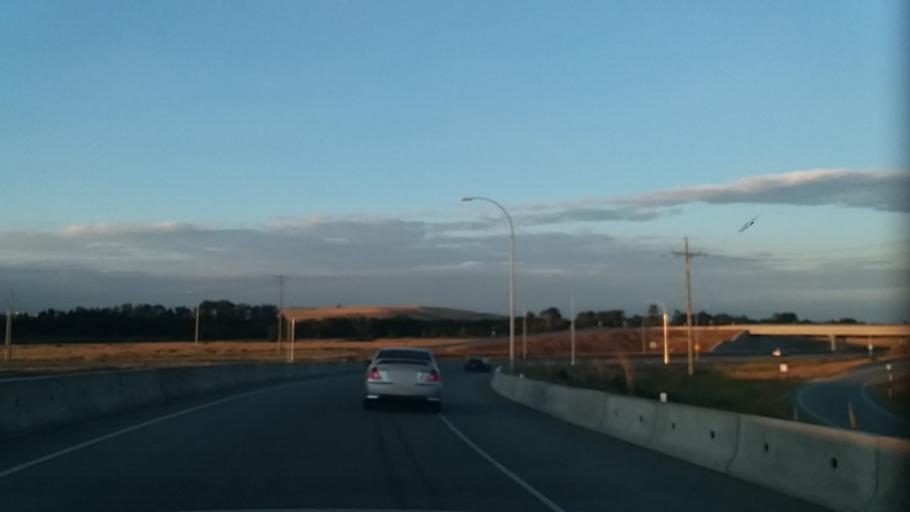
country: CA
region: British Columbia
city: Ladner
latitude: 49.0935
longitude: -123.0227
